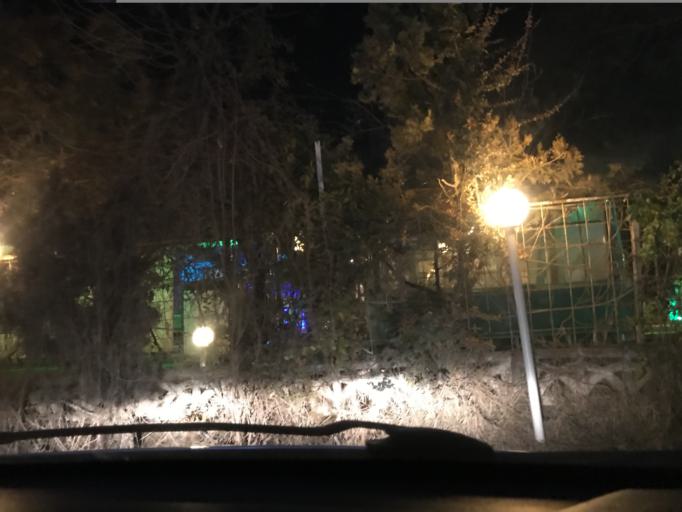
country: TR
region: Ankara
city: Etimesgut
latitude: 40.0557
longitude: 32.6264
